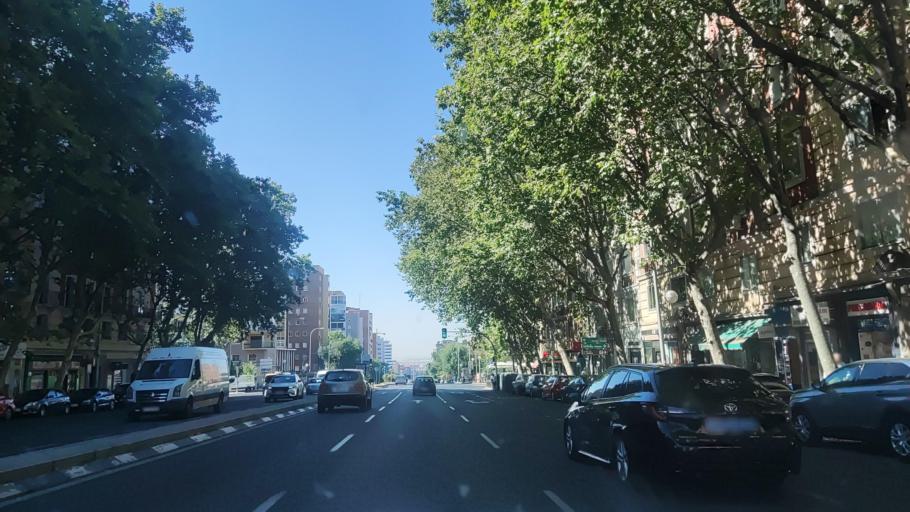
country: ES
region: Madrid
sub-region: Provincia de Madrid
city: Retiro
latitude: 40.4175
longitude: -3.6693
